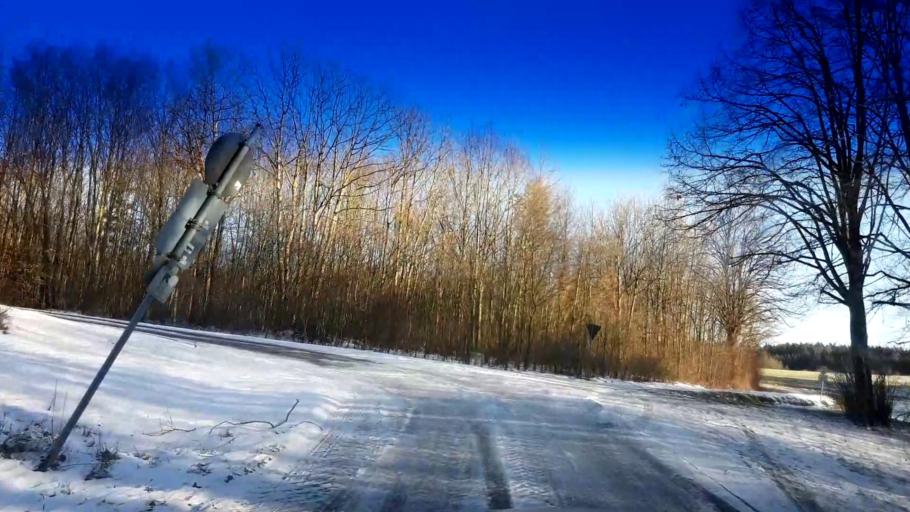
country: DE
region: Bavaria
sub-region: Upper Franconia
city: Buttenheim
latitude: 49.8348
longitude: 11.0858
